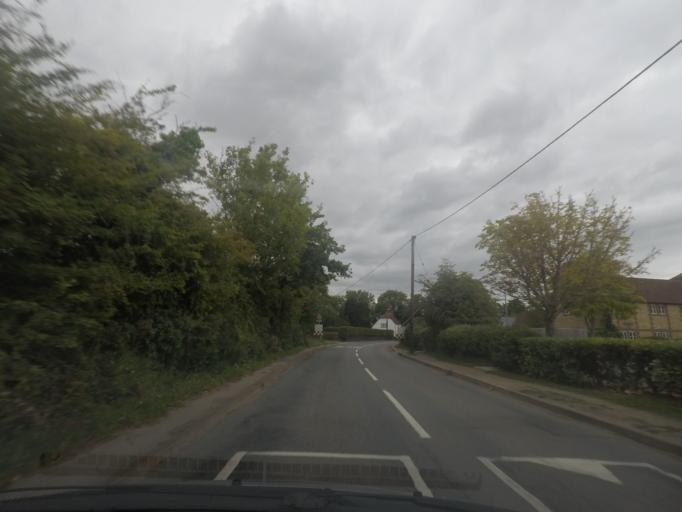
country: GB
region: England
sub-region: Oxfordshire
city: Harwell
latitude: 51.6242
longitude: -1.3024
